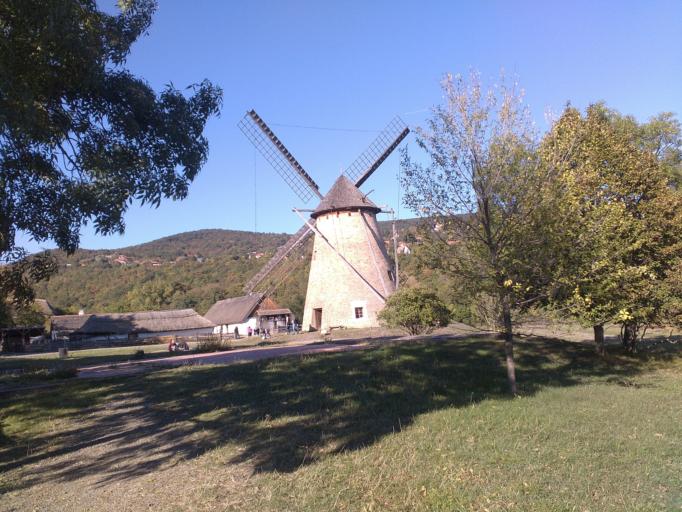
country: HU
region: Pest
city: Szentendre
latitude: 47.6948
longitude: 19.0462
